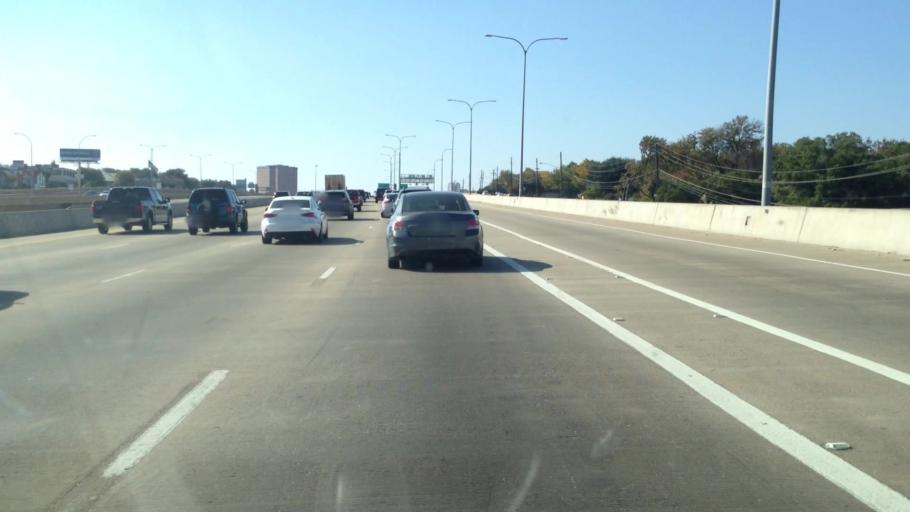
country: US
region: Texas
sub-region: Dallas County
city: Addison
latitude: 32.9256
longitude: -96.7896
